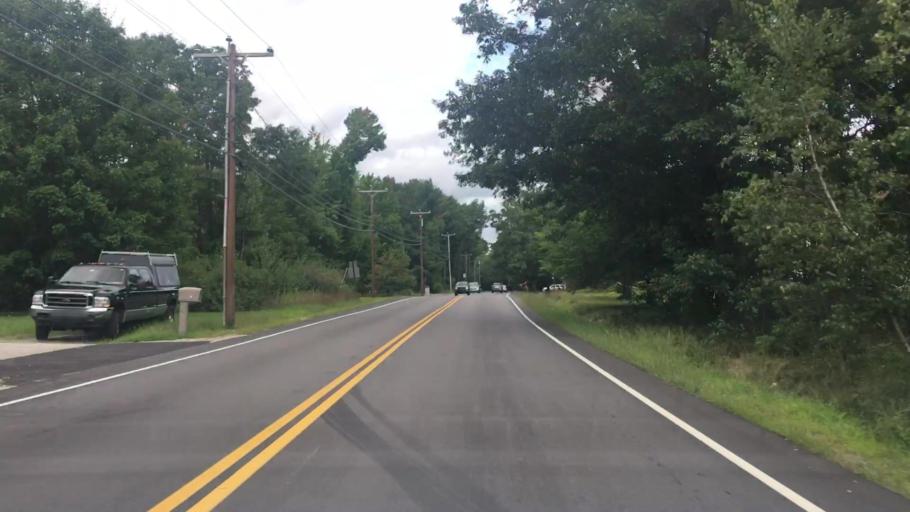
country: US
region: Maine
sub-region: York County
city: Dayton
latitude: 43.4809
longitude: -70.6037
